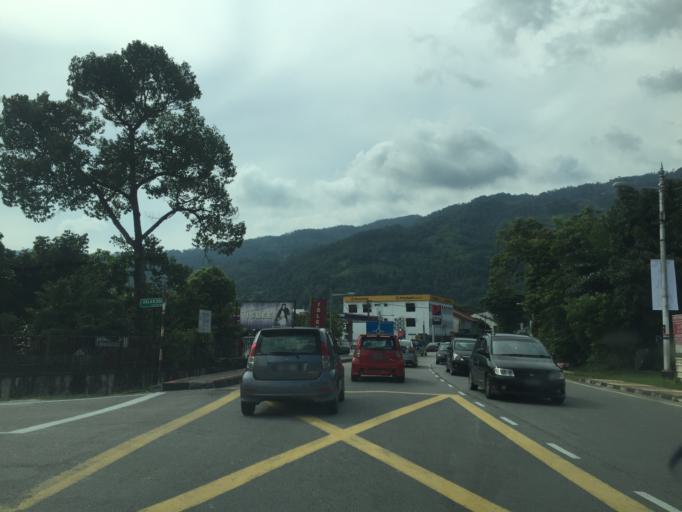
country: MY
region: Penang
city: George Town
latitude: 5.4043
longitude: 100.2854
